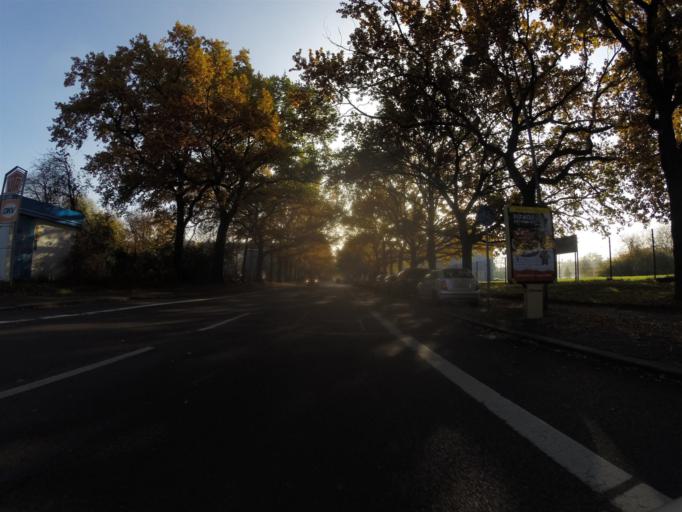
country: DE
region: Saxony
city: Leipzig
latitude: 51.3400
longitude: 12.3542
